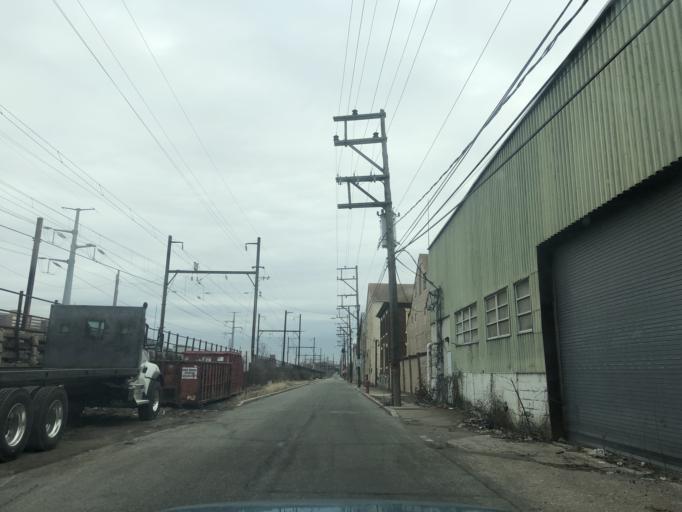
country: US
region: Pennsylvania
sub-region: Montgomery County
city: Bridgeport
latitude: 40.1116
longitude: -75.3412
